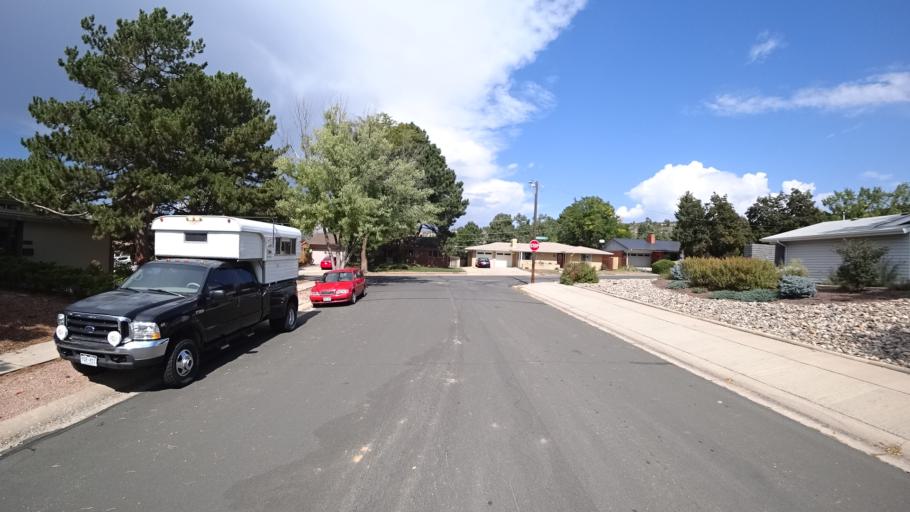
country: US
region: Colorado
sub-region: El Paso County
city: Colorado Springs
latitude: 38.8661
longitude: -104.7699
